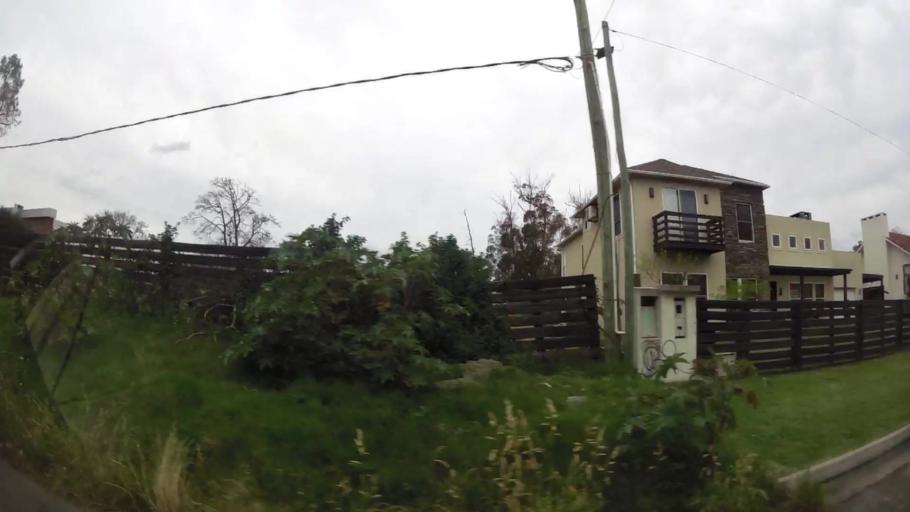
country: UY
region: Maldonado
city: Maldonado
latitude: -34.9156
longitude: -54.9728
